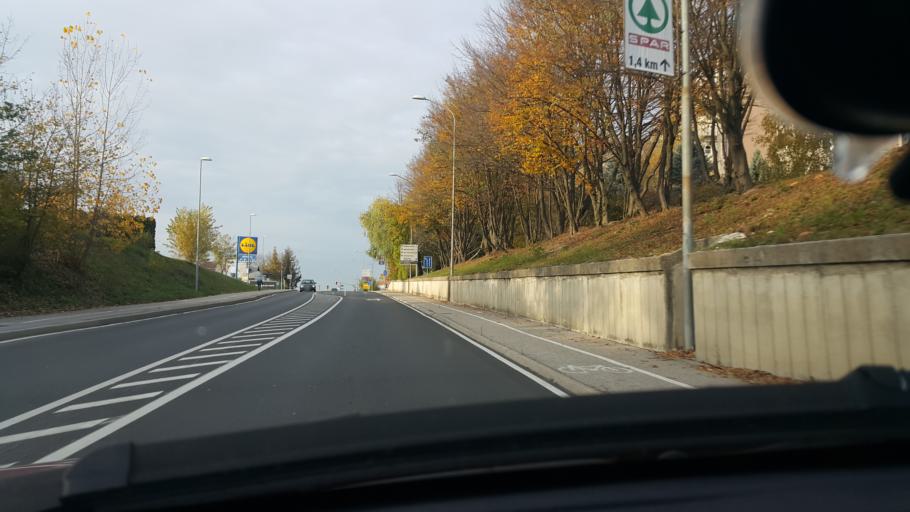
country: SI
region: Brezice
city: Brezice
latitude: 45.9037
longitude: 15.6036
